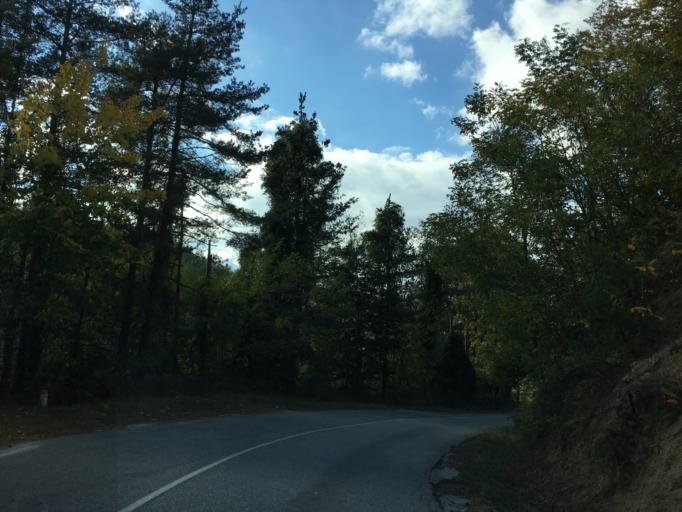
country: BG
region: Smolyan
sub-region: Obshtina Madan
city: Madan
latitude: 41.4608
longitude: 24.9700
